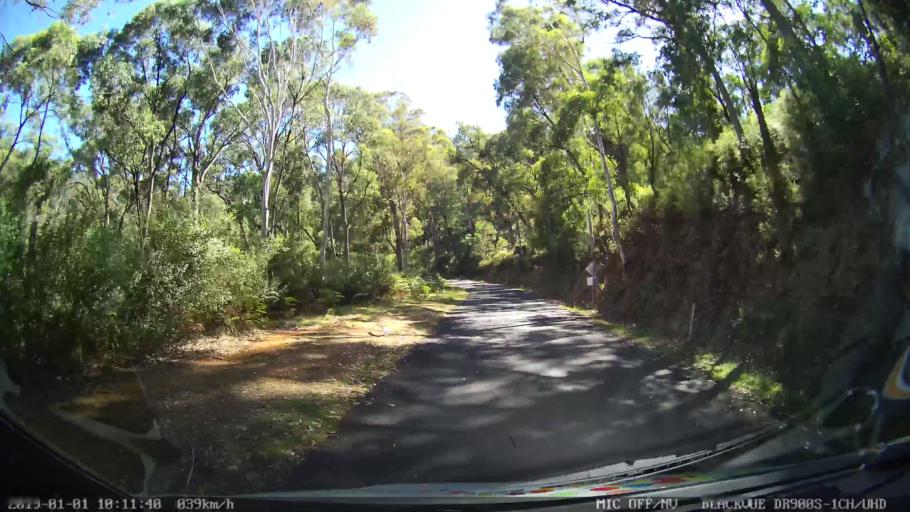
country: AU
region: New South Wales
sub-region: Snowy River
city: Jindabyne
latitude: -36.1359
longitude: 148.1557
